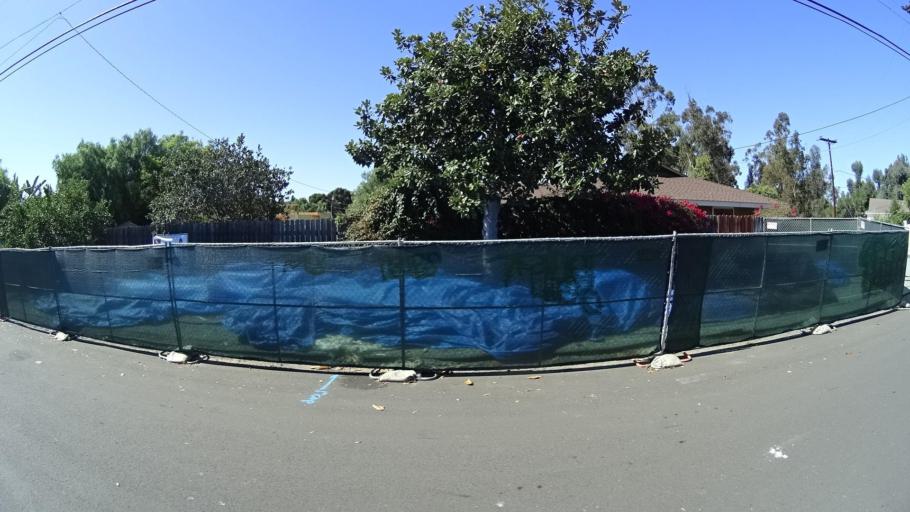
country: US
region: California
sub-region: San Diego County
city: Chula Vista
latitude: 32.6411
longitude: -117.0600
